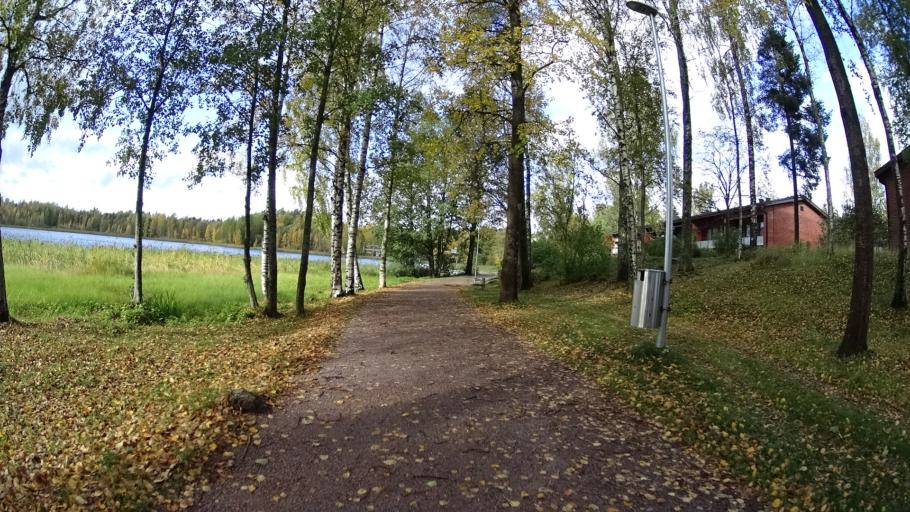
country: FI
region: Uusimaa
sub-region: Helsinki
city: Kilo
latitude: 60.2596
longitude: 24.8019
